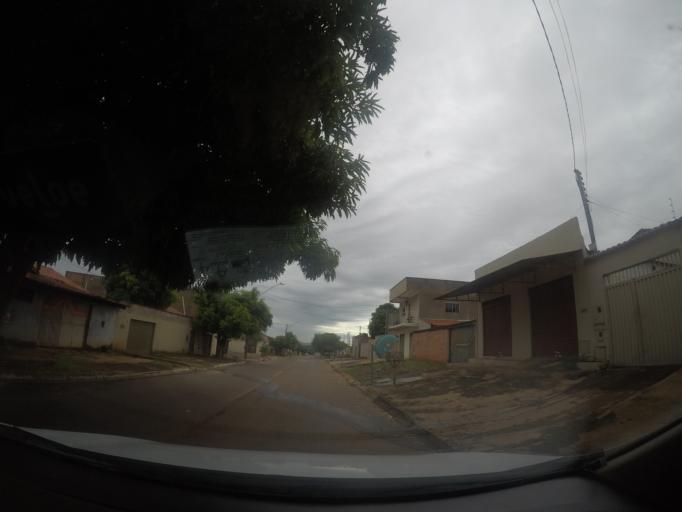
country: BR
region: Goias
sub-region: Goiania
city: Goiania
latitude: -16.6114
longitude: -49.3110
